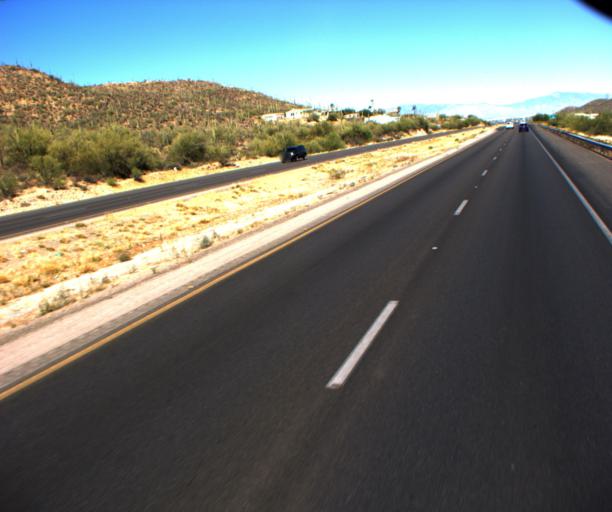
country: US
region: Arizona
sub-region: Pima County
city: Drexel Heights
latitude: 32.1768
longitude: -111.0317
